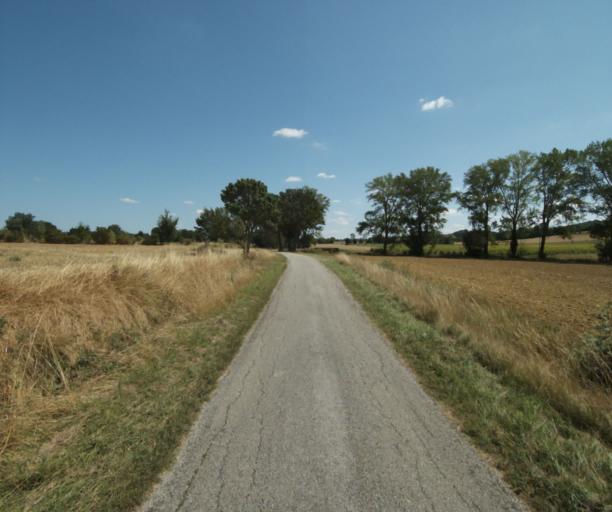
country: FR
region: Midi-Pyrenees
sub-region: Departement de la Haute-Garonne
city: Saint-Felix-Lauragais
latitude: 43.4911
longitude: 1.8715
